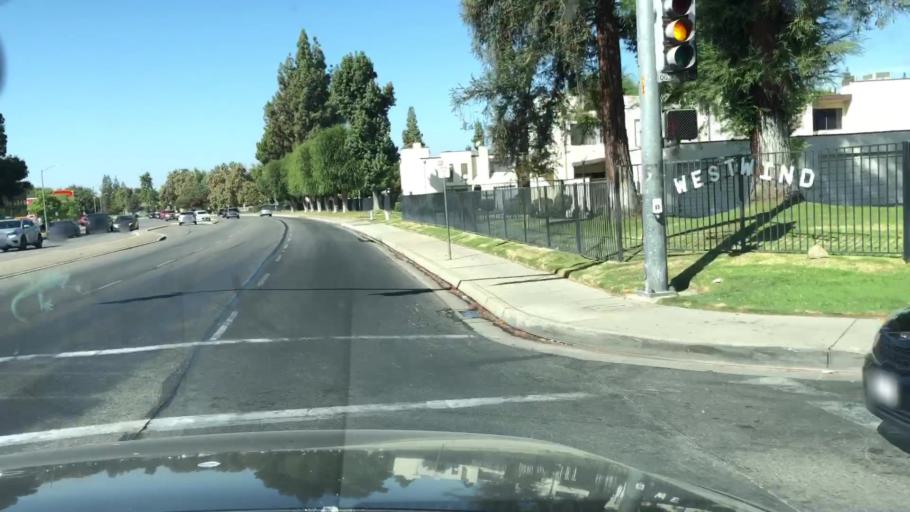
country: US
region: California
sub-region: Kern County
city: Bakersfield
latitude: 35.3397
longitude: -119.0552
